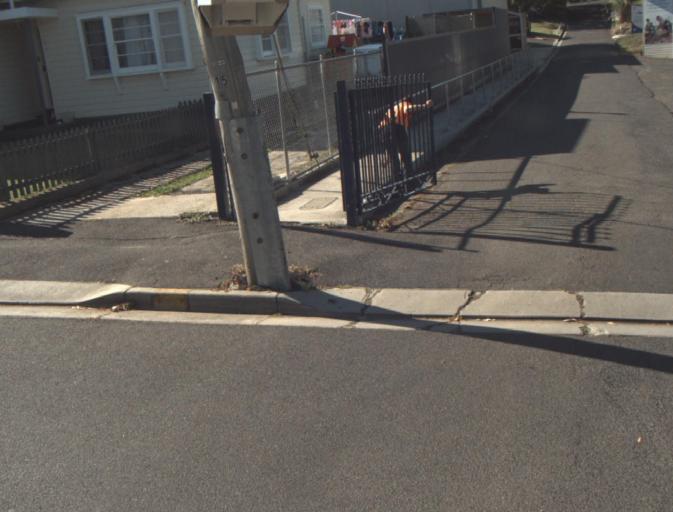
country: AU
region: Tasmania
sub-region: Launceston
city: Newnham
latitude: -41.4067
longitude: 147.1256
